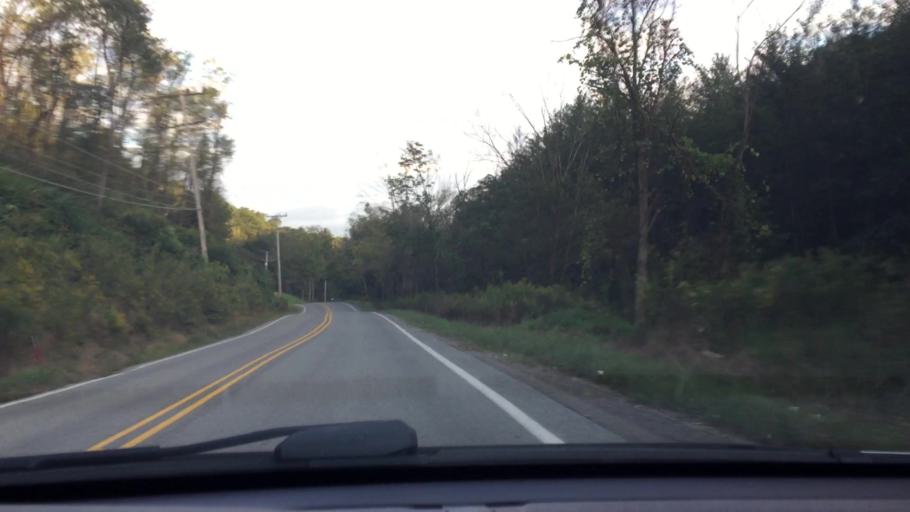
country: US
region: Pennsylvania
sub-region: Westmoreland County
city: Murrysville
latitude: 40.4509
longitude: -79.7264
